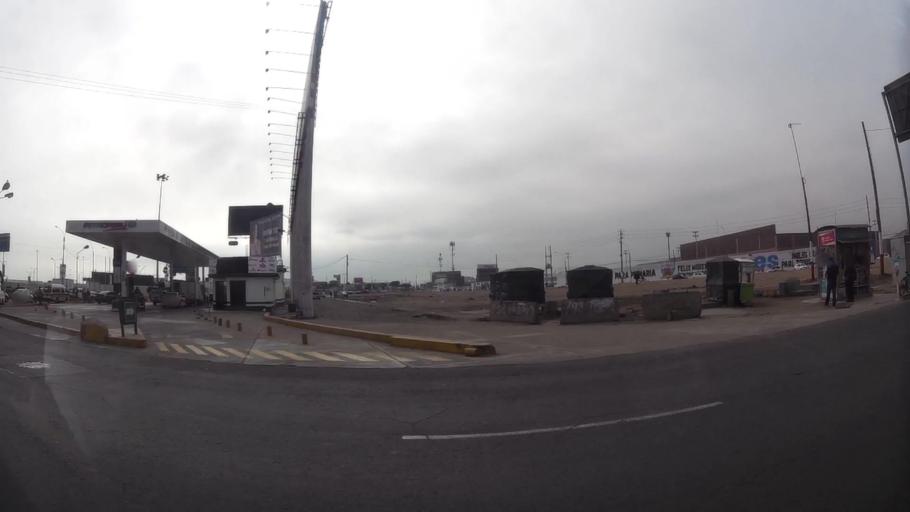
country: PE
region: Callao
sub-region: Callao
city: Callao
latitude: -12.0215
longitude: -77.1055
